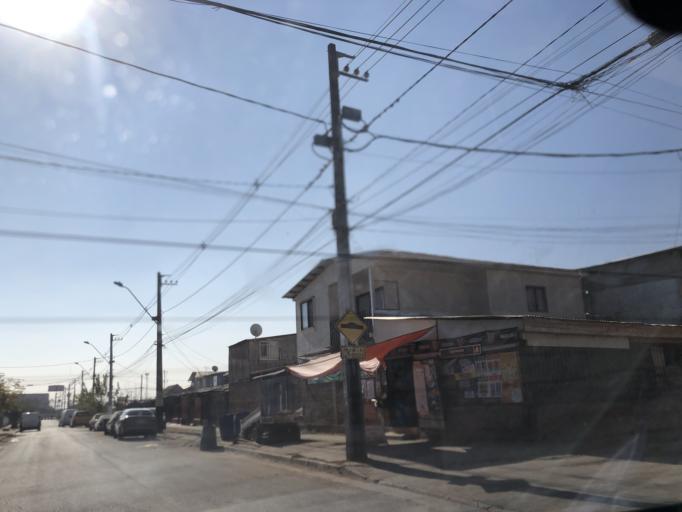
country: CL
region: Santiago Metropolitan
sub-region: Provincia de Cordillera
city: Puente Alto
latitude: -33.6181
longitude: -70.5973
